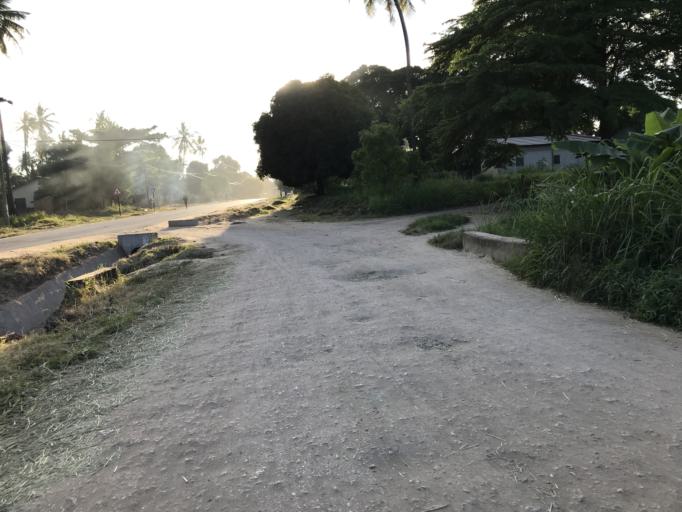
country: TZ
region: Dar es Salaam
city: Dar es Salaam
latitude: -6.8634
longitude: 39.3603
